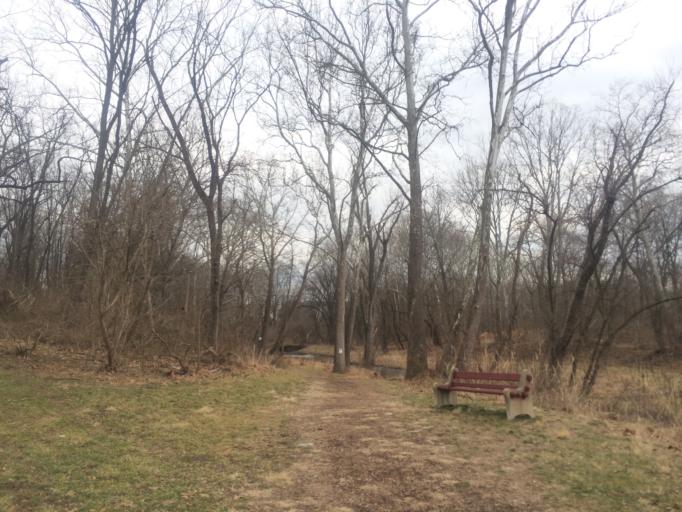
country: US
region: Pennsylvania
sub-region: Lebanon County
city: Annville
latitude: 40.3274
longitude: -76.5064
